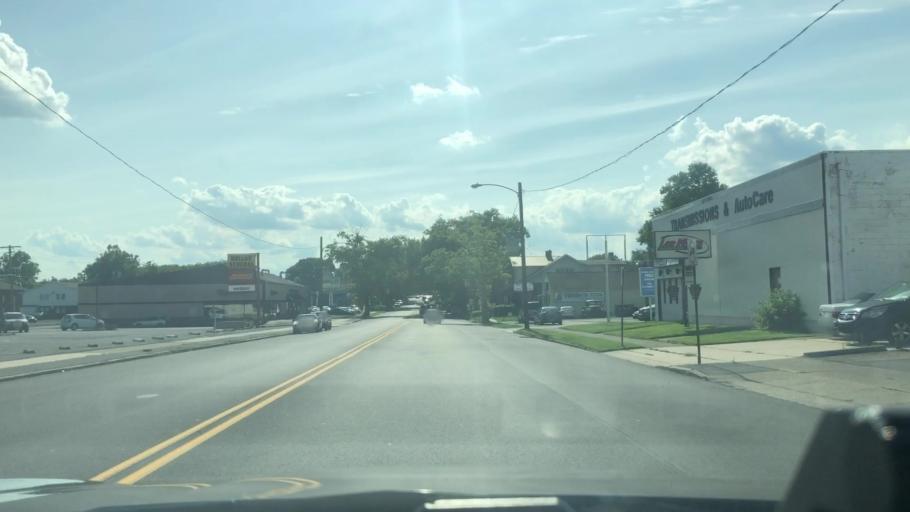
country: US
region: Pennsylvania
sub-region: Lehigh County
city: Fountain Hill
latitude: 40.6259
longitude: -75.4237
